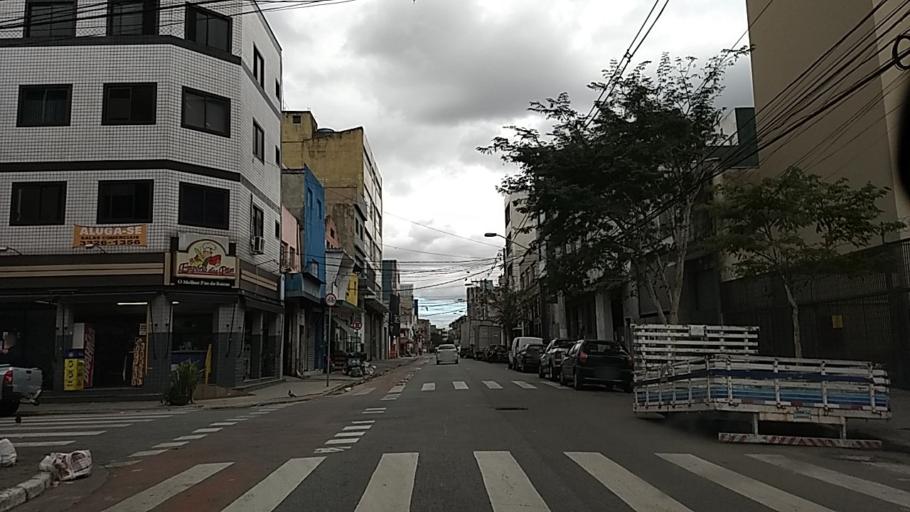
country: BR
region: Sao Paulo
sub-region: Sao Paulo
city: Sao Paulo
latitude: -23.5300
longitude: -46.6230
